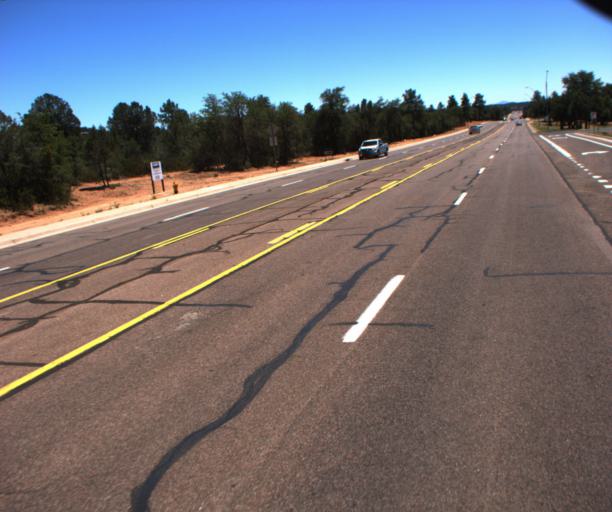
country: US
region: Arizona
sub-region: Gila County
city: Payson
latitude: 34.2647
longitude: -111.3222
